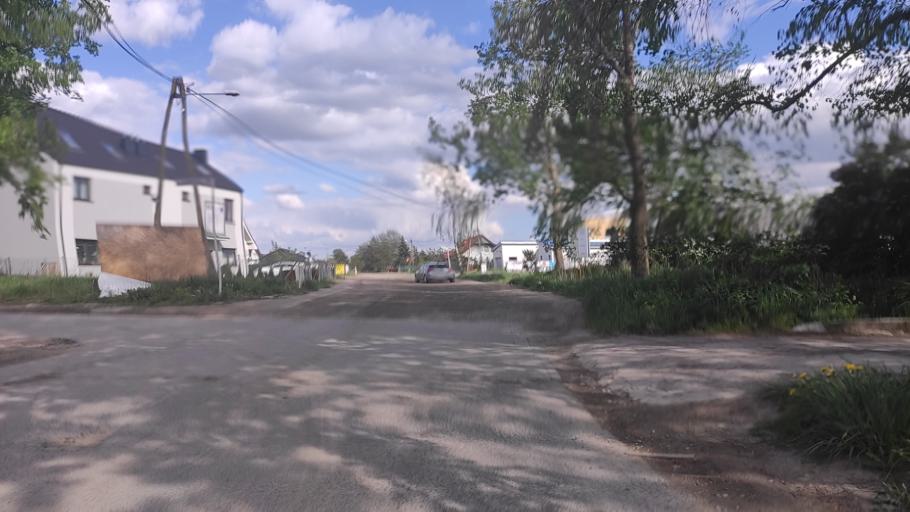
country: PL
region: Greater Poland Voivodeship
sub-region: Powiat poznanski
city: Swarzedz
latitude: 52.3903
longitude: 17.1197
